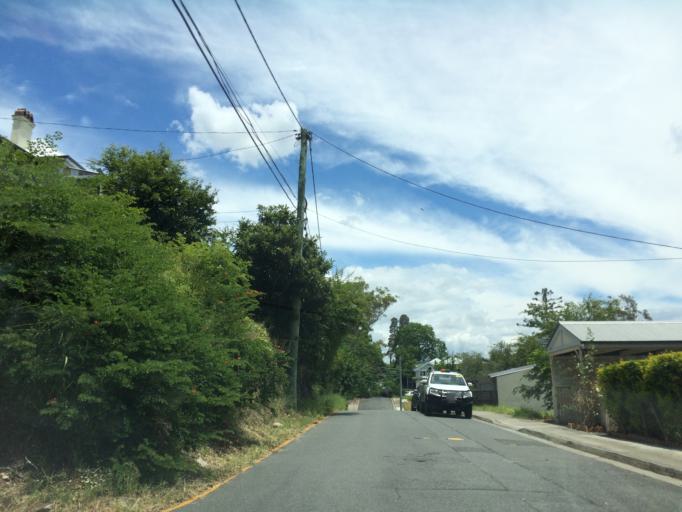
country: AU
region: Queensland
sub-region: Brisbane
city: South Brisbane
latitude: -27.4880
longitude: 153.0143
